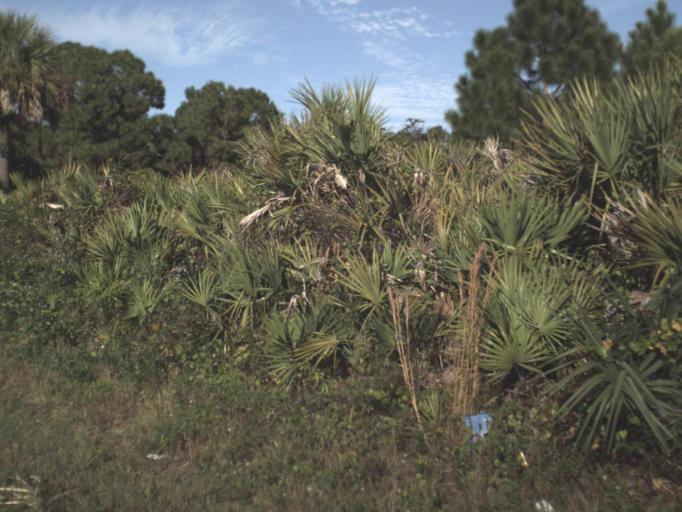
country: US
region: Florida
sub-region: Brevard County
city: June Park
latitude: 28.1094
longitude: -80.6725
